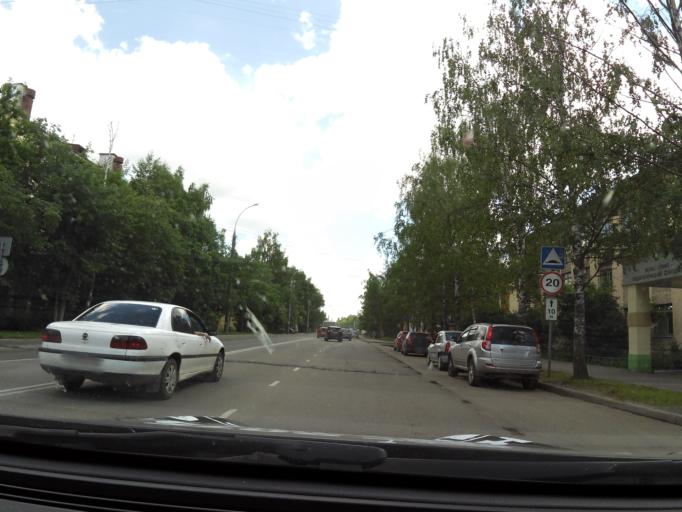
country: RU
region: Vologda
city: Vologda
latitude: 59.2249
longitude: 39.8706
